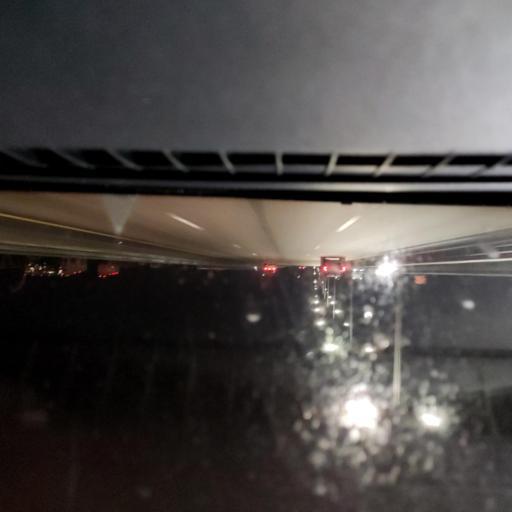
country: RU
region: Voronezj
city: Somovo
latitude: 51.7312
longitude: 39.3111
